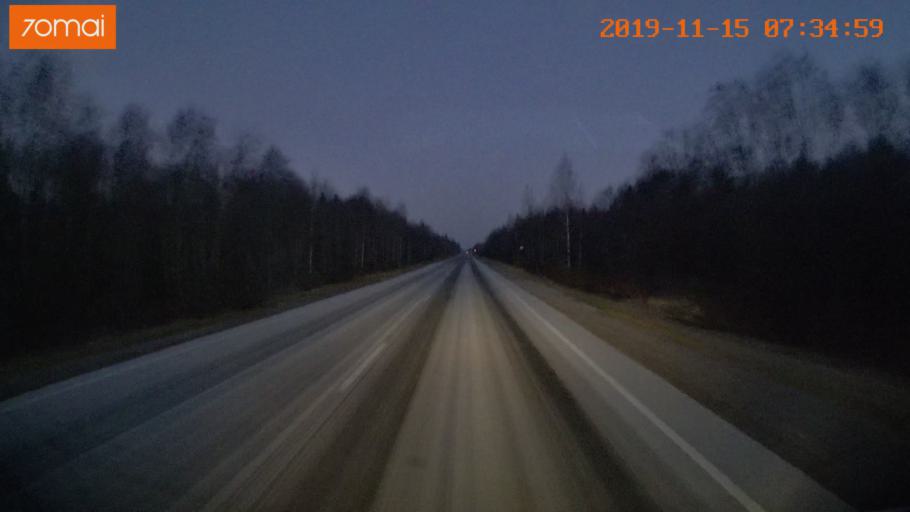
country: RU
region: Vologda
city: Sheksna
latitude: 58.7266
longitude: 38.4588
